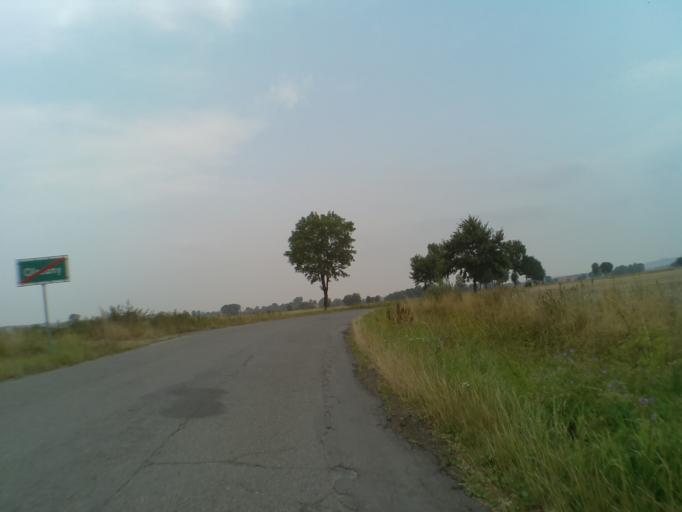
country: PL
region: Lower Silesian Voivodeship
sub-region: Powiat swidnicki
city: Swiebodzice
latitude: 50.9043
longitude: 16.3179
